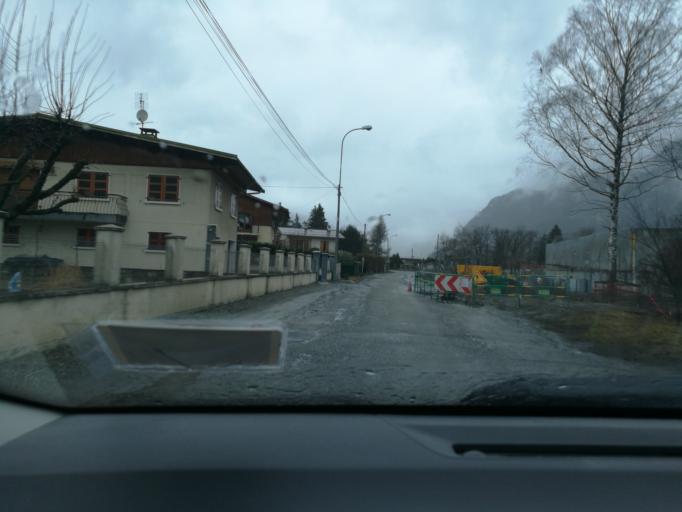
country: FR
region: Rhone-Alpes
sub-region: Departement de la Haute-Savoie
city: Domancy
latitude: 45.9293
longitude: 6.6454
